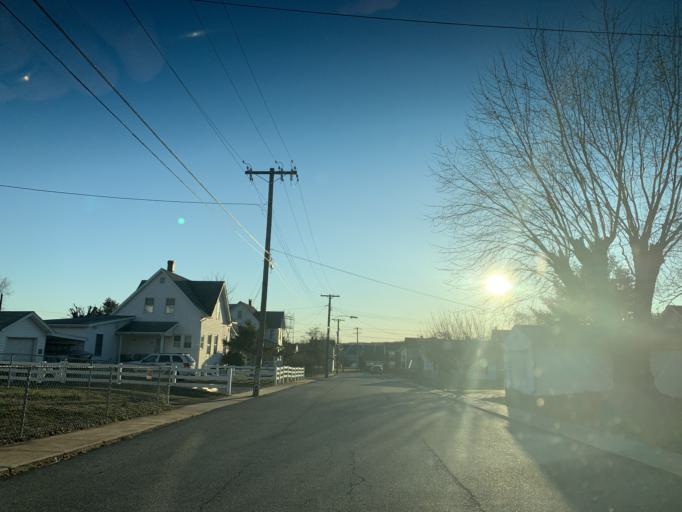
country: US
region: Maryland
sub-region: Cecil County
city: Perryville
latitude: 39.5612
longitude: -76.0769
